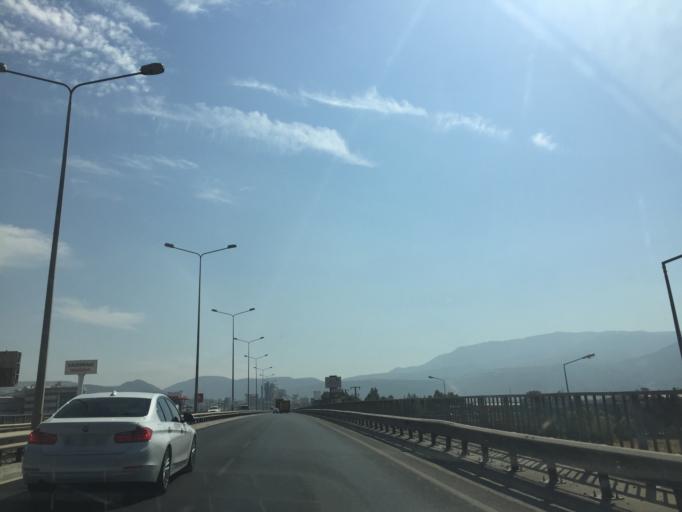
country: TR
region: Izmir
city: Bornova
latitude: 38.4587
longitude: 27.2444
